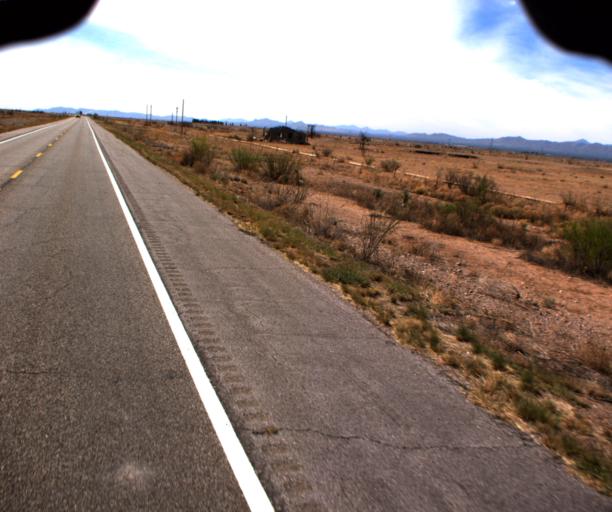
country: US
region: Arizona
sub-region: Cochise County
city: Pirtleville
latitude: 31.5719
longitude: -109.6682
